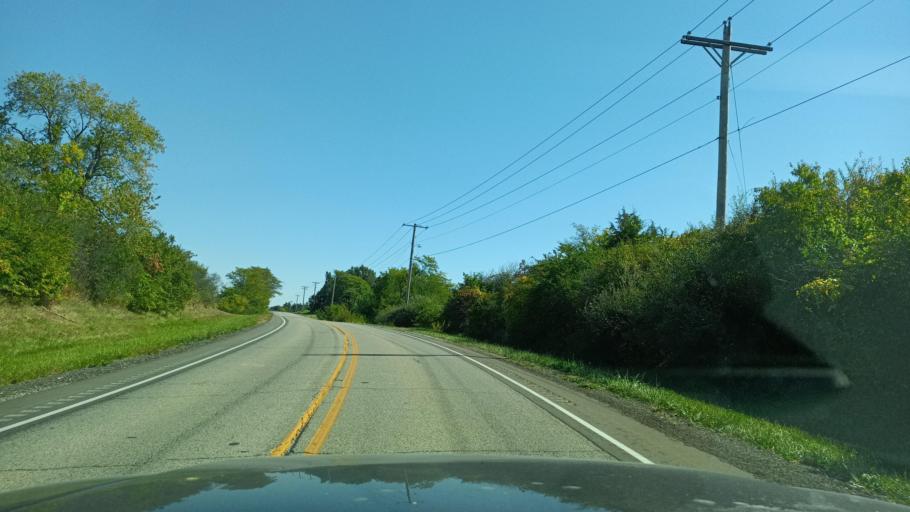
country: US
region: Illinois
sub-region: McLean County
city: Danvers
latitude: 40.6168
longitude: -89.2347
